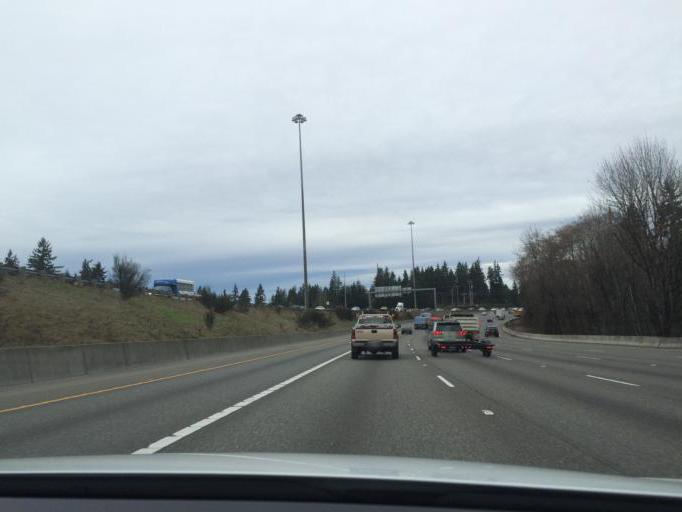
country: US
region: Washington
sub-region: Snohomish County
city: Everett
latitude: 47.9247
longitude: -122.2039
